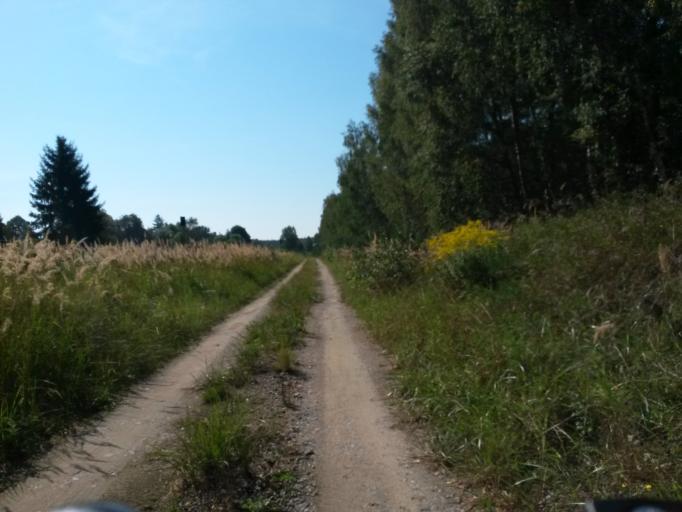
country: DE
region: Brandenburg
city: Zehdenick
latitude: 53.0372
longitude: 13.3850
